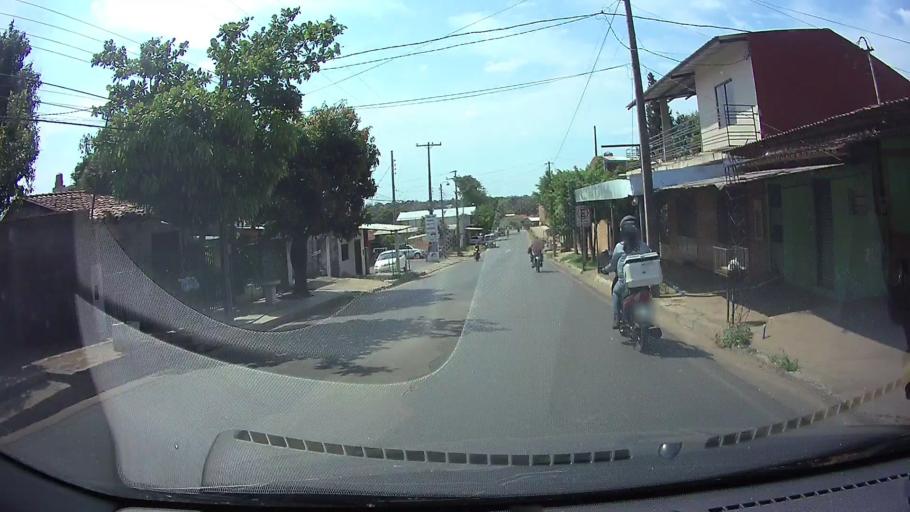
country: PY
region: Central
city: San Lorenzo
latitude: -25.3330
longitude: -57.4923
